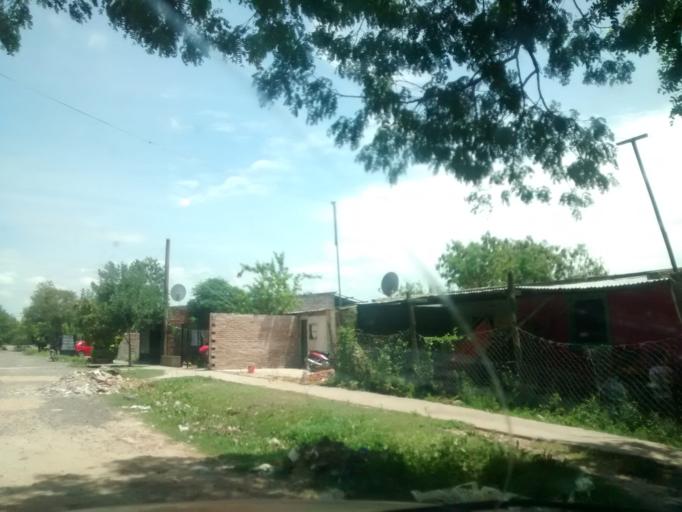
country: AR
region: Chaco
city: Resistencia
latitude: -27.4346
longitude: -58.9745
